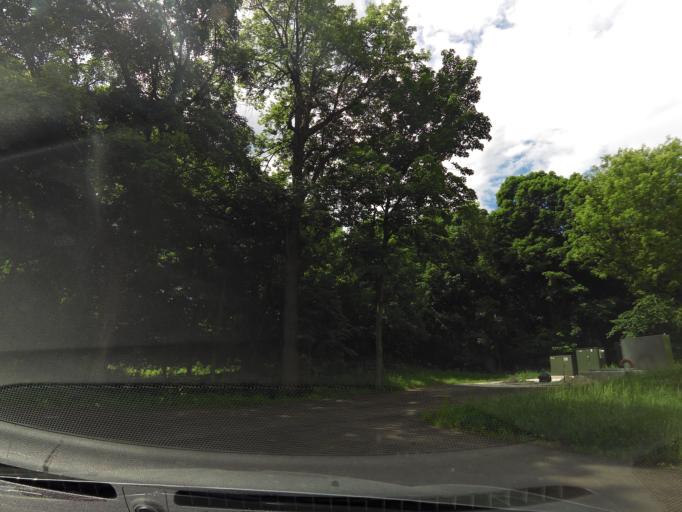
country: US
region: Minnesota
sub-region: Scott County
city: Prior Lake
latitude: 44.7534
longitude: -93.4579
